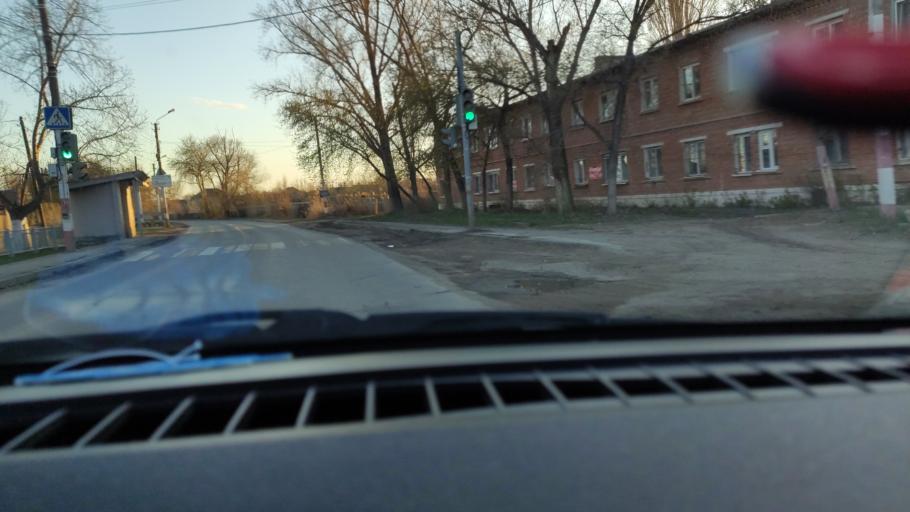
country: RU
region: Saratov
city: Engel's
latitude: 51.4949
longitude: 46.0574
